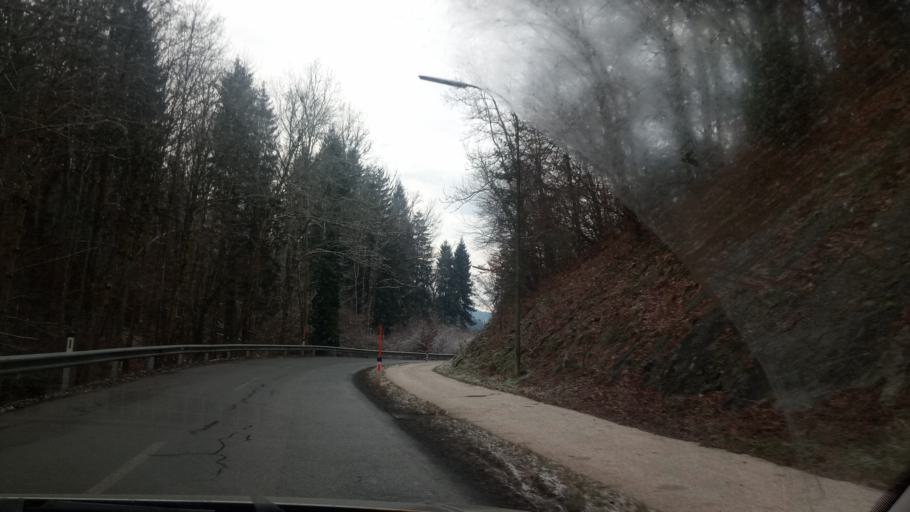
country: AT
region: Carinthia
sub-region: Politischer Bezirk Klagenfurt Land
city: Kottmannsdorf
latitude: 46.5905
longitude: 14.2628
